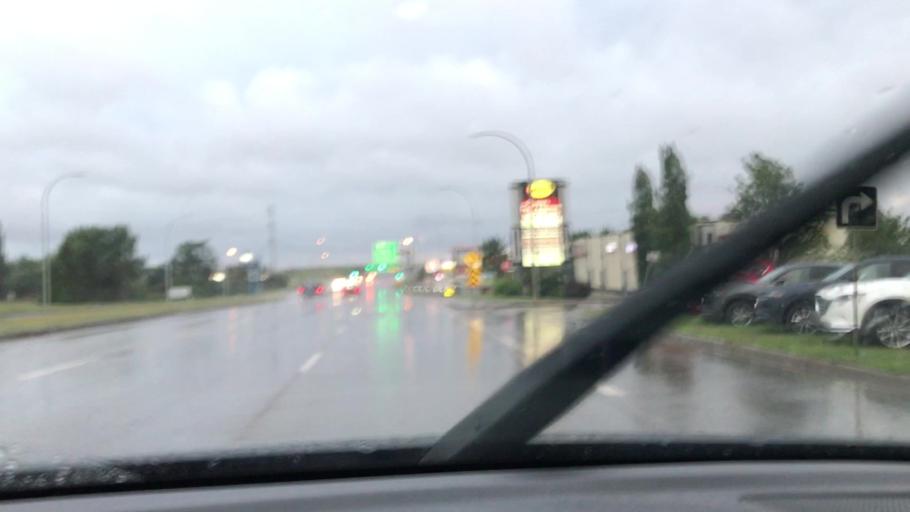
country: CA
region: Alberta
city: Sherwood Park
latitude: 53.5120
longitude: -113.3265
